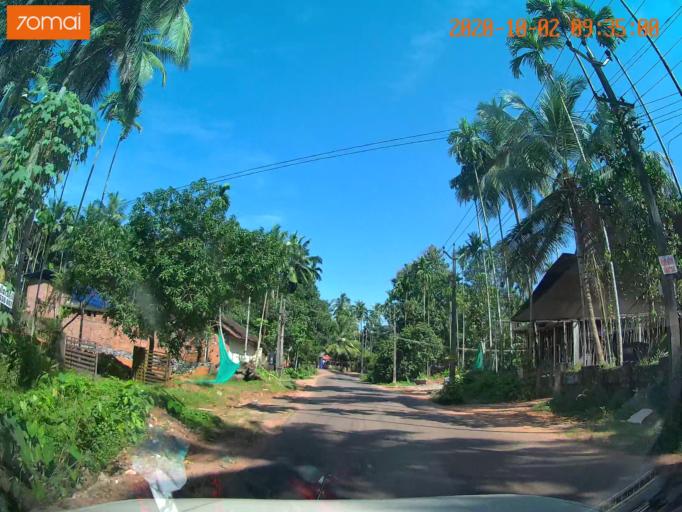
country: IN
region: Kerala
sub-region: Kozhikode
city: Nadapuram
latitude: 11.6417
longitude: 75.7549
